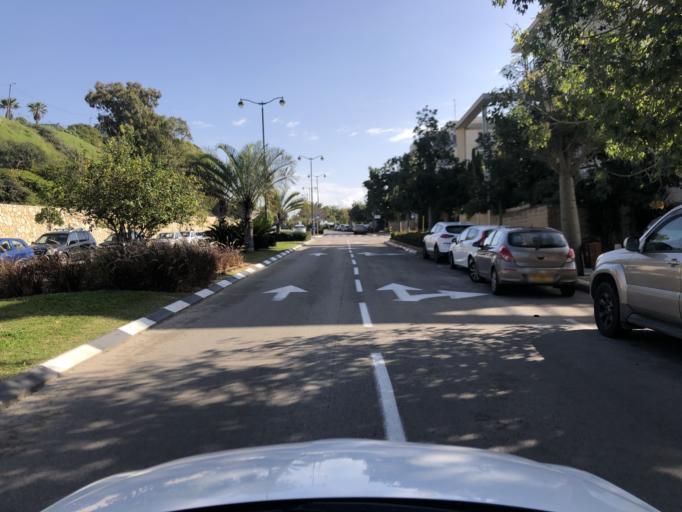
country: IL
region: Central District
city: Ness Ziona
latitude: 31.9145
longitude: 34.7906
